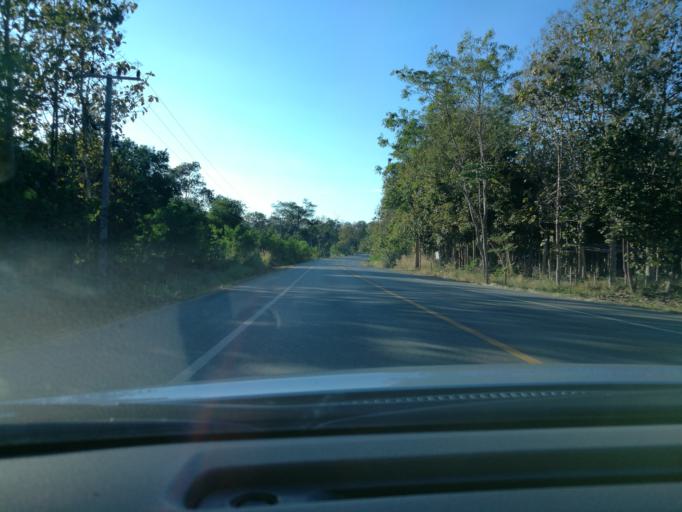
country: TH
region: Phitsanulok
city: Nakhon Thai
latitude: 17.0695
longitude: 100.8405
